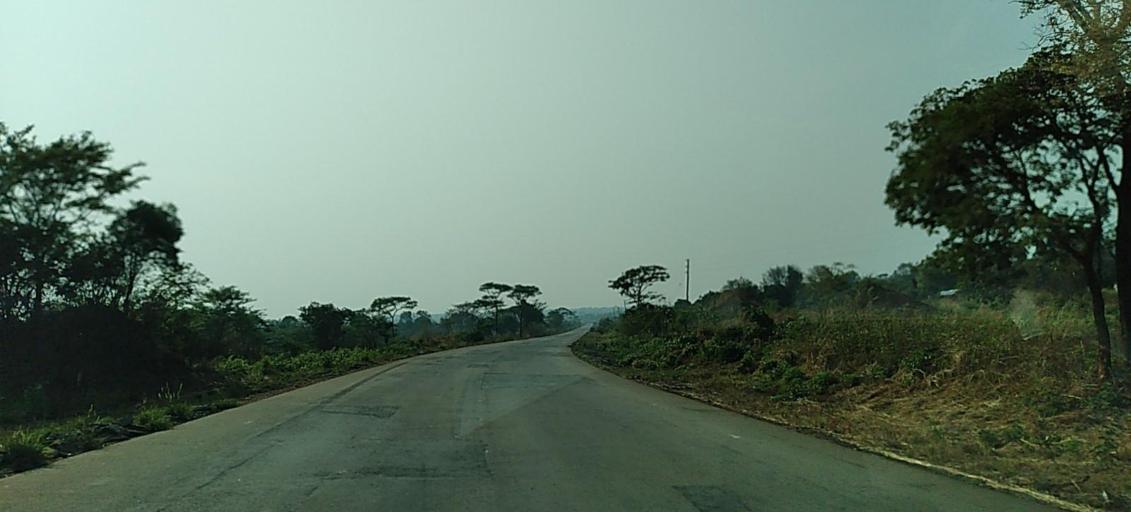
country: ZM
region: North-Western
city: Kansanshi
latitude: -12.2990
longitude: 26.9282
